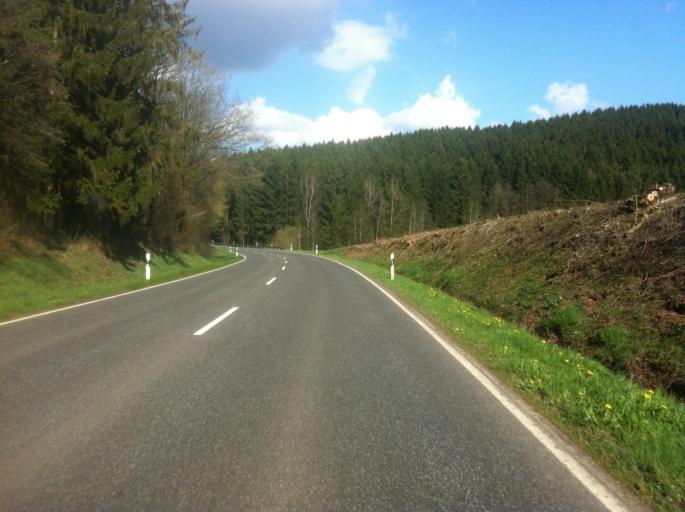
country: DE
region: Rheinland-Pfalz
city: Watzerath
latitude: 50.1858
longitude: 6.3734
